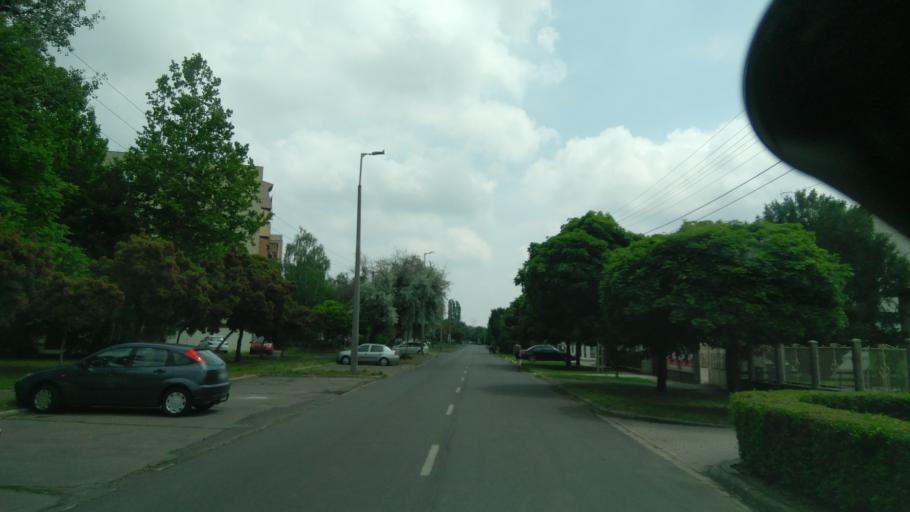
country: HU
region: Bekes
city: Gyula
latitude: 46.6554
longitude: 21.2607
